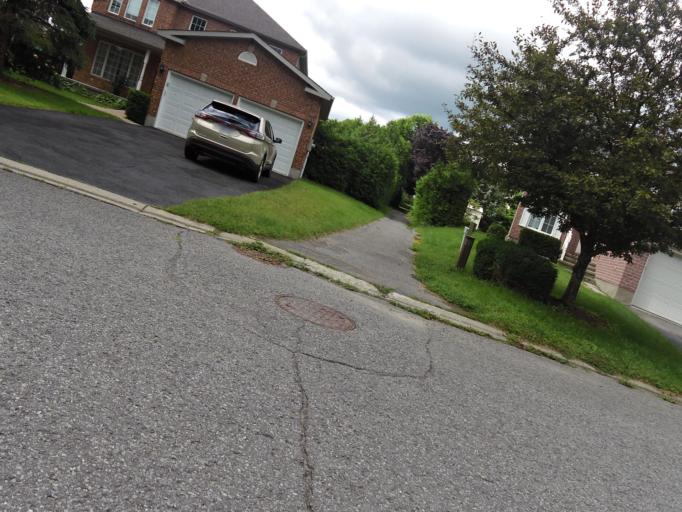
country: CA
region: Ontario
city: Bells Corners
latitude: 45.3234
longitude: -75.9202
